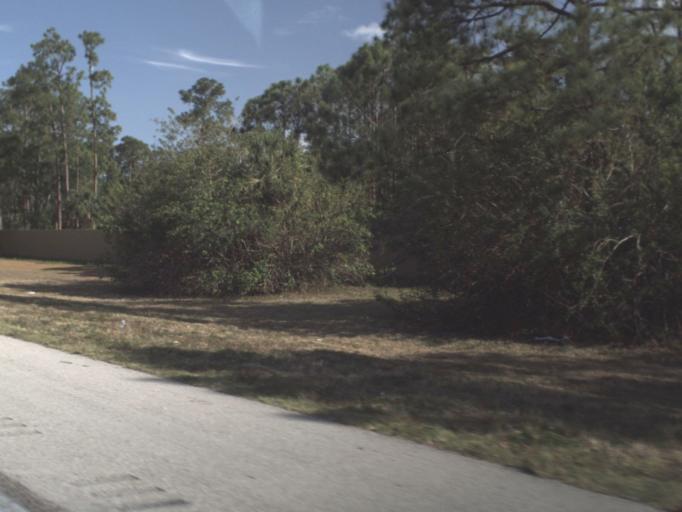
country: US
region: Florida
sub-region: Brevard County
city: June Park
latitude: 28.0520
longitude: -80.6763
